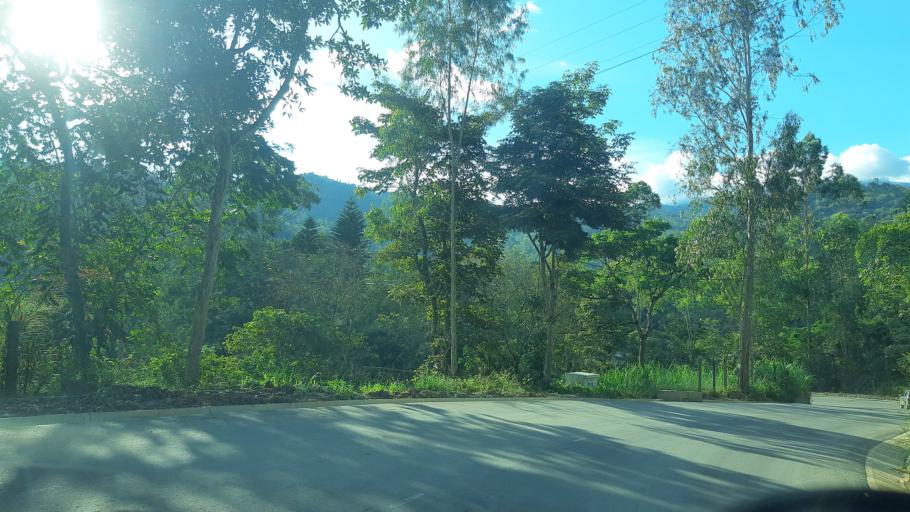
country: CO
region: Boyaca
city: Garagoa
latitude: 5.0841
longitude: -73.3817
